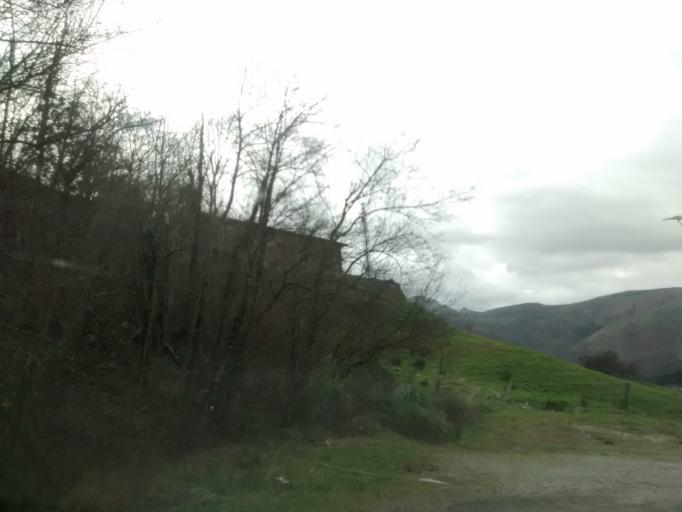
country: ES
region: Cantabria
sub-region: Provincia de Cantabria
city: Lierganes
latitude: 43.3304
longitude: -3.7389
